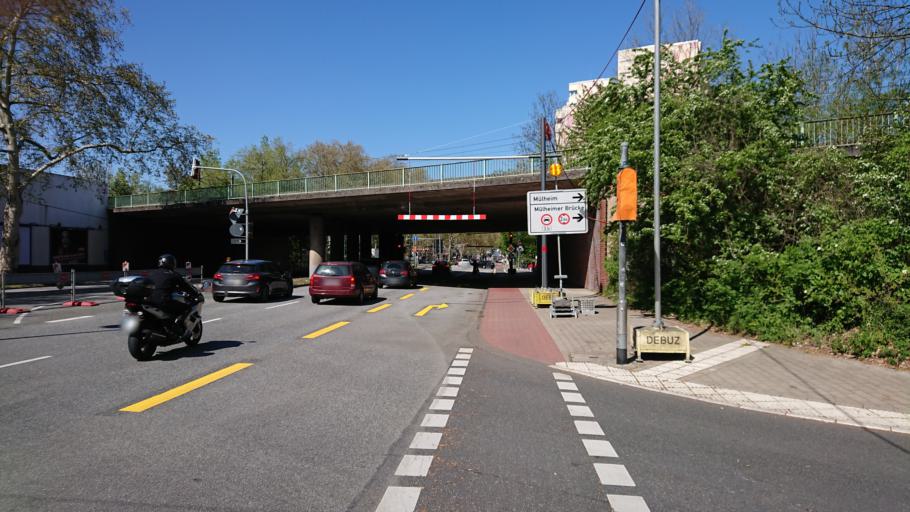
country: DE
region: North Rhine-Westphalia
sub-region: Regierungsbezirk Koln
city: Riehl
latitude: 50.9694
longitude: 6.9780
